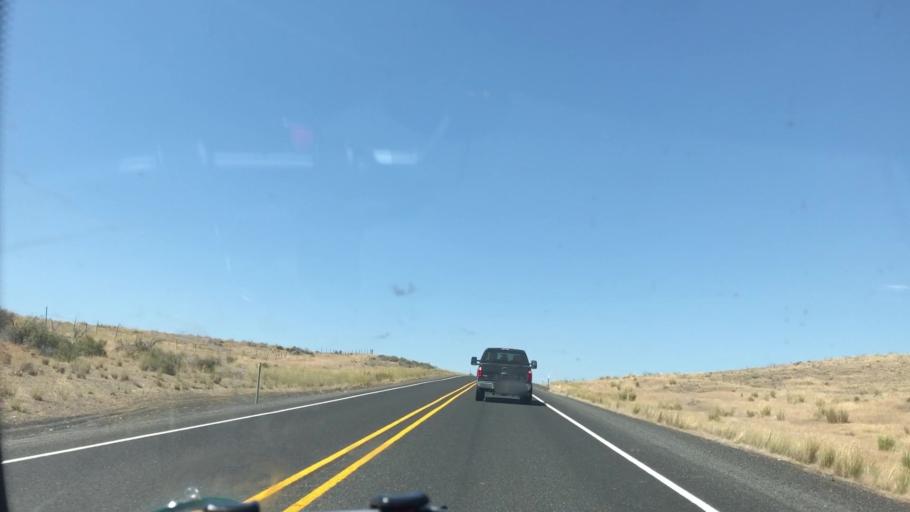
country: US
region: Idaho
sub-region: Owyhee County
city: Marsing
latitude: 43.2350
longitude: -117.0460
